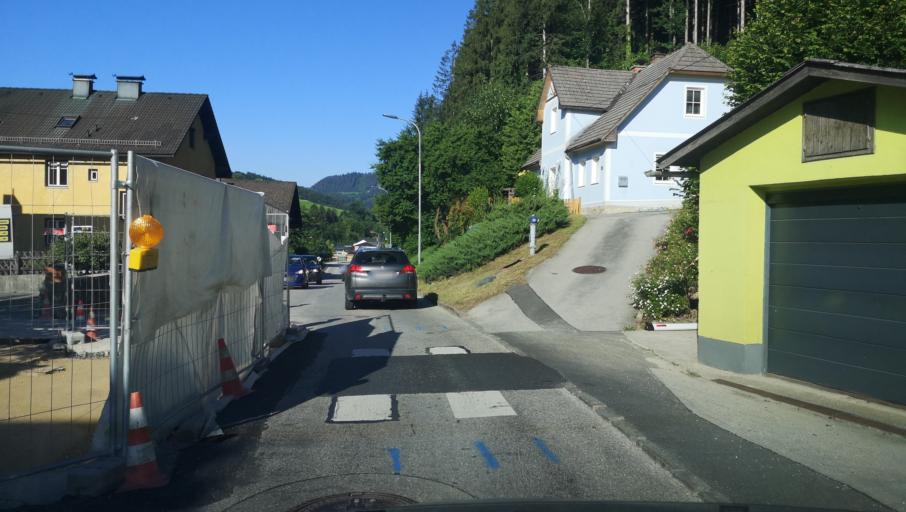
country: AT
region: Lower Austria
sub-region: Politischer Bezirk Amstetten
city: Ybbsitz
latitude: 47.9476
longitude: 14.8872
